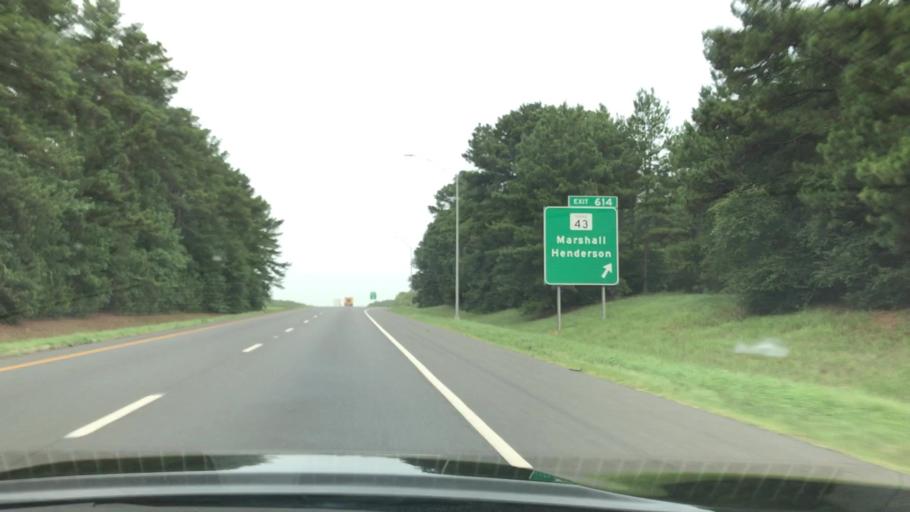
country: US
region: Texas
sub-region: Harrison County
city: Marshall
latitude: 32.4894
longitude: -94.4033
